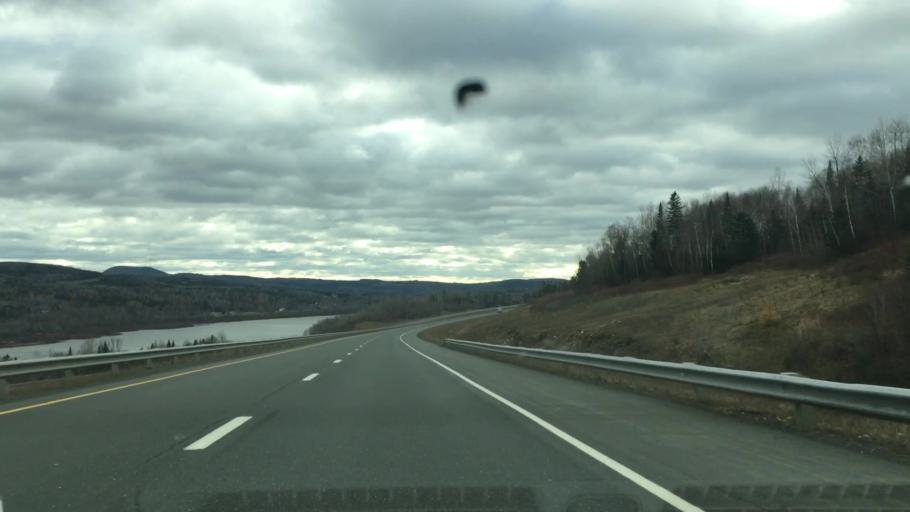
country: US
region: Maine
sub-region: Aroostook County
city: Fort Fairfield
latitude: 46.6827
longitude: -67.7332
